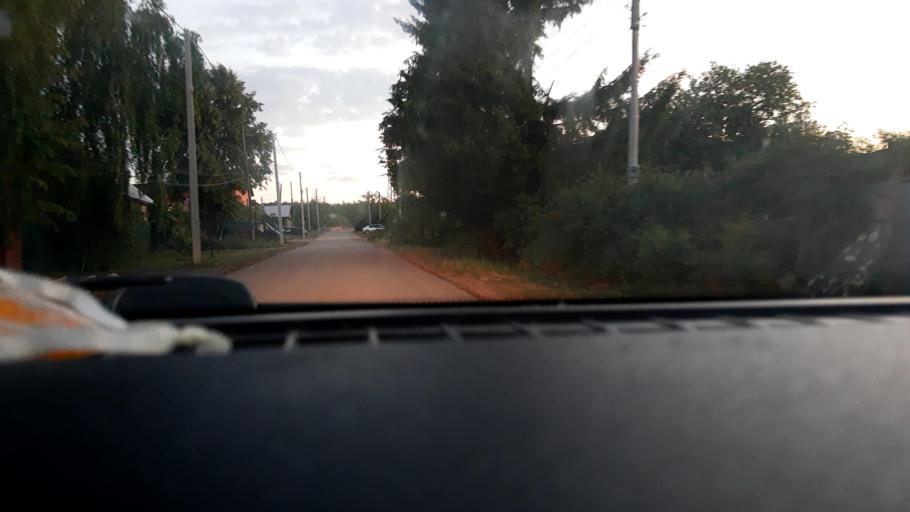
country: RU
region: Bashkortostan
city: Avdon
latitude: 54.6189
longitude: 55.6447
